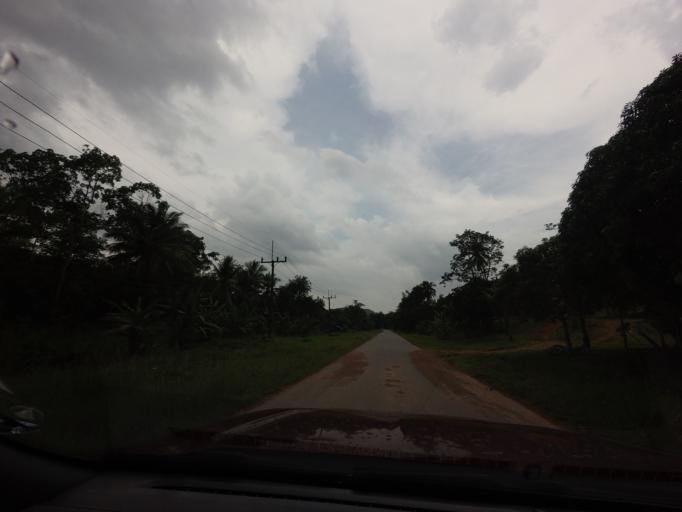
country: TH
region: Yala
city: Ban Nang Sata
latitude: 6.2081
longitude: 101.2348
